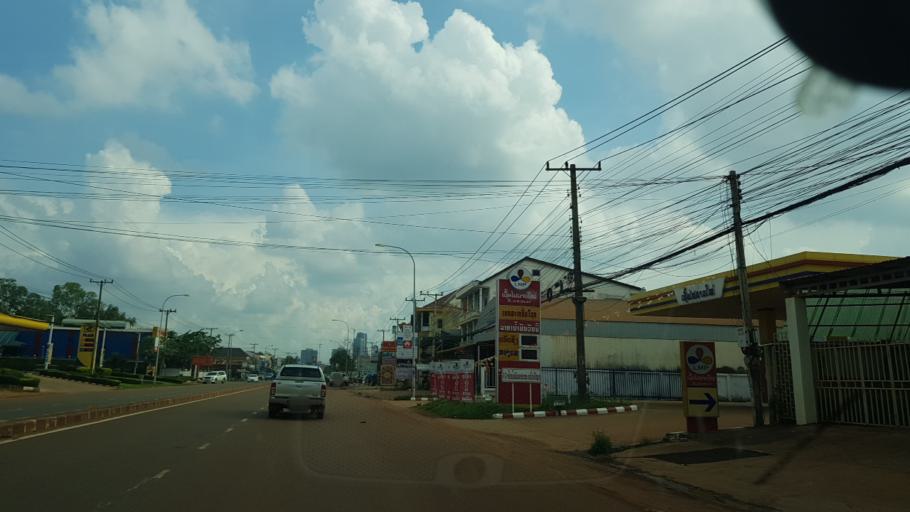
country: LA
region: Vientiane
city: Vientiane
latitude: 18.0179
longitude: 102.6505
